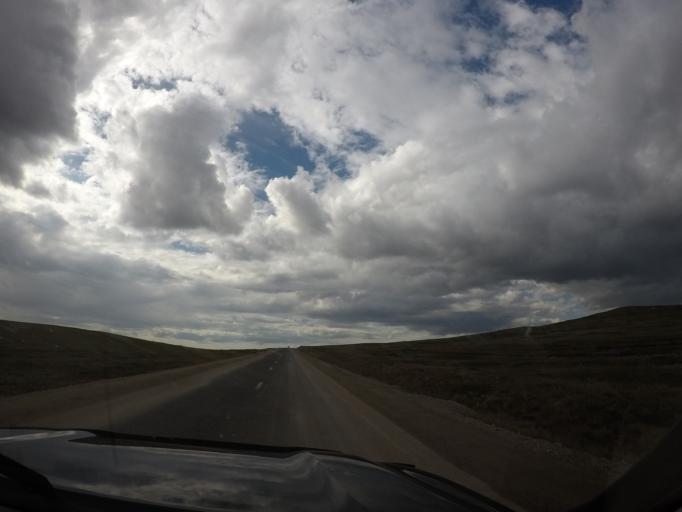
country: MN
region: Hentiy
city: Modot
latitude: 47.5484
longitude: 109.3717
